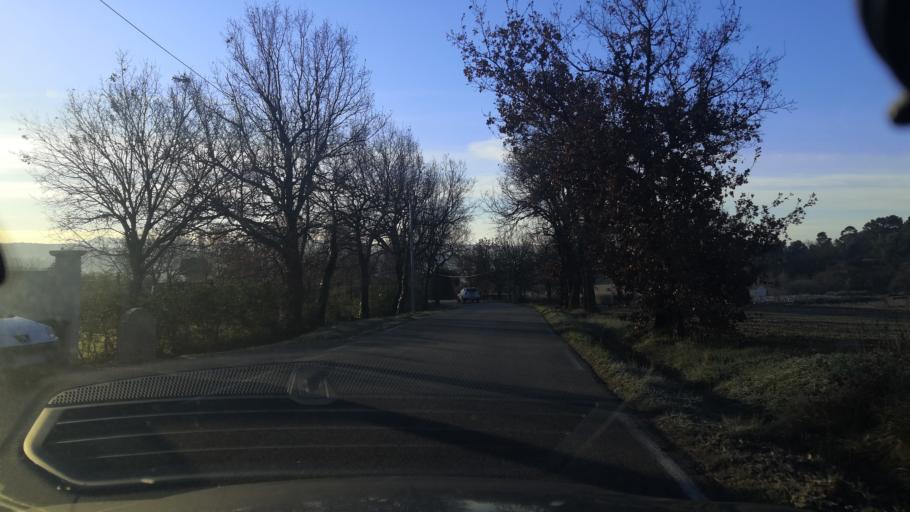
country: FR
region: Provence-Alpes-Cote d'Azur
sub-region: Departement des Bouches-du-Rhone
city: Aix-en-Provence
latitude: 43.5172
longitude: 5.4057
